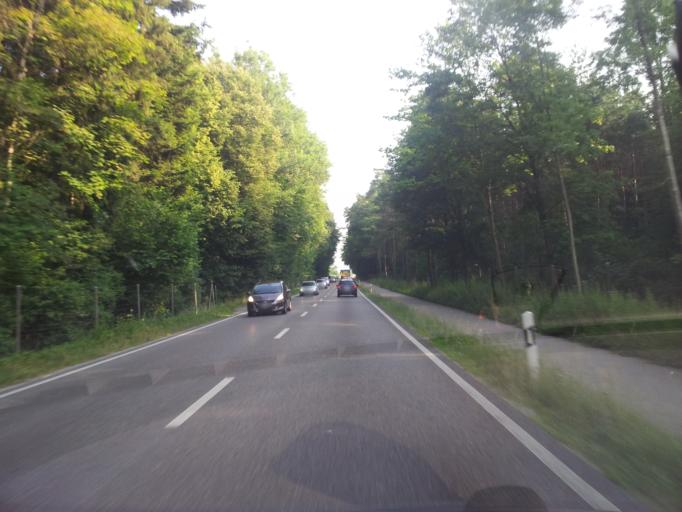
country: CH
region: Zurich
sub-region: Bezirk Buelach
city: Buelach / Soligaenter
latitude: 47.5458
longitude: 8.5306
